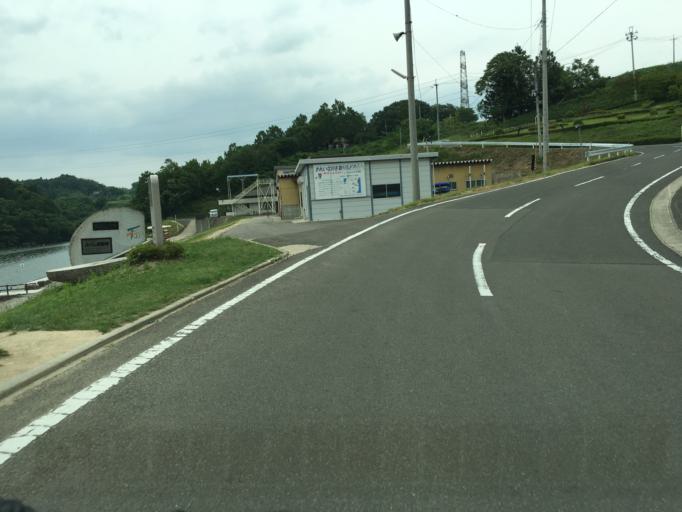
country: JP
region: Fukushima
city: Nihommatsu
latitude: 37.6307
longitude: 140.5242
